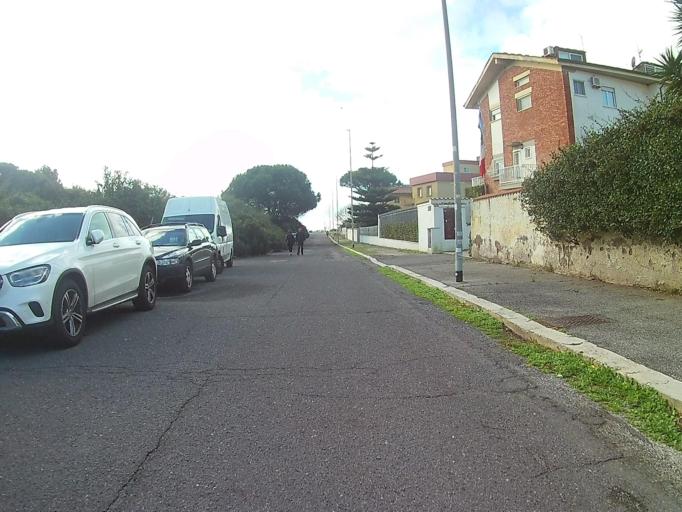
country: IT
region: Latium
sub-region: Citta metropolitana di Roma Capitale
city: Lido di Ostia
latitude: 41.7214
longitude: 12.3063
